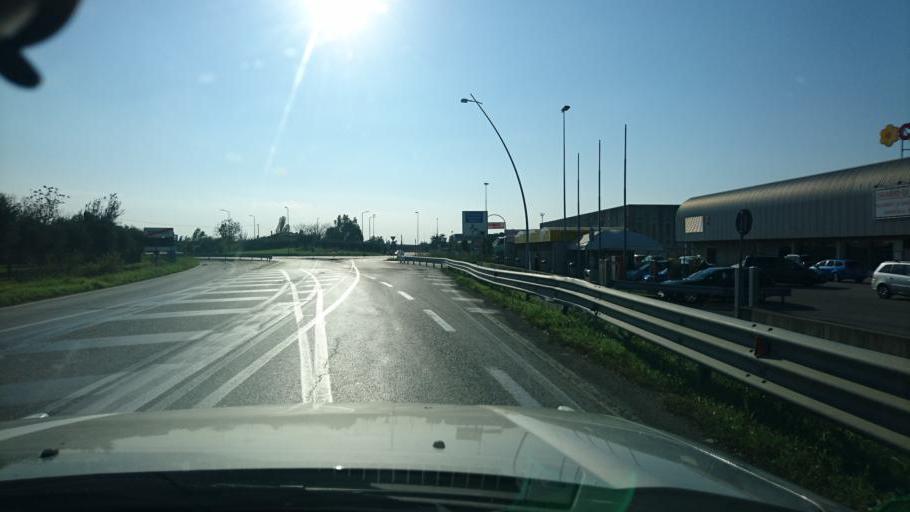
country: IT
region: Veneto
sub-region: Provincia di Padova
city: Monselice
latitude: 45.2140
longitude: 11.7552
